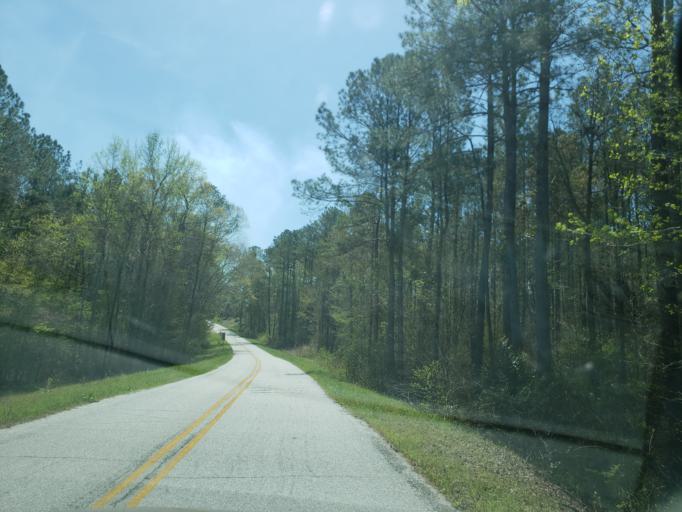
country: US
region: Alabama
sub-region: Elmore County
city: Tallassee
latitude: 32.6722
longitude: -85.8615
